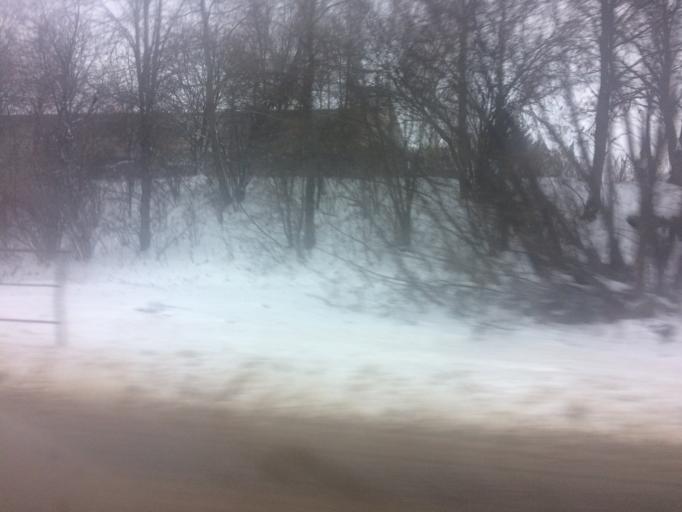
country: RU
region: Tula
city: Tula
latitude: 54.1638
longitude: 37.6222
